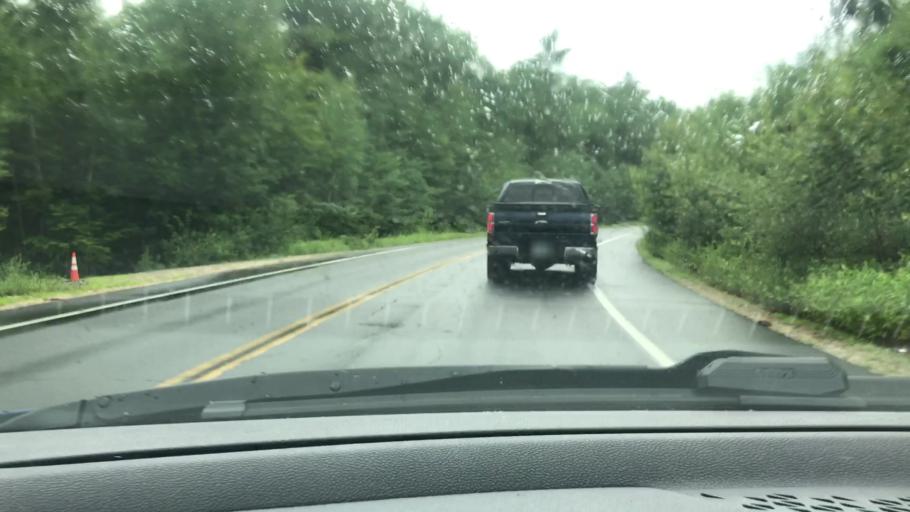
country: US
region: New Hampshire
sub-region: Rockingham County
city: Candia
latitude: 43.1384
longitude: -71.2359
